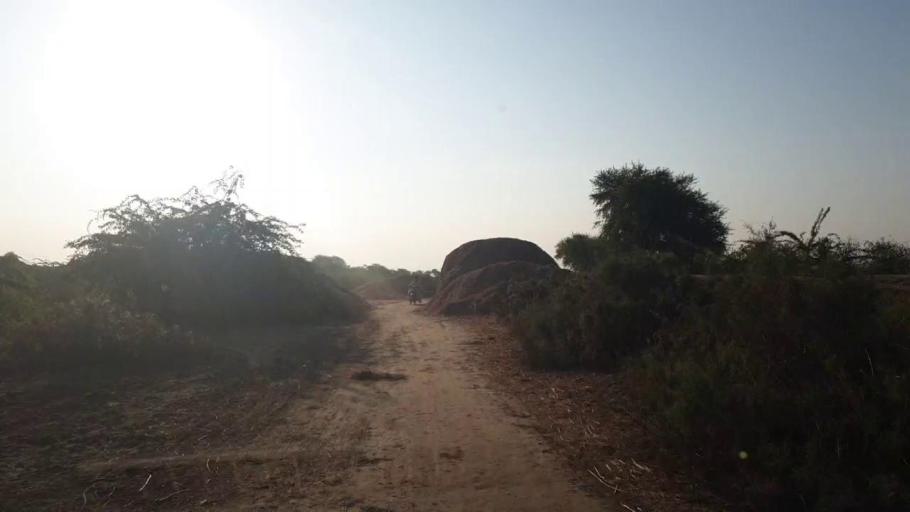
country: PK
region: Sindh
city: Badin
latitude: 24.6360
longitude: 68.7936
